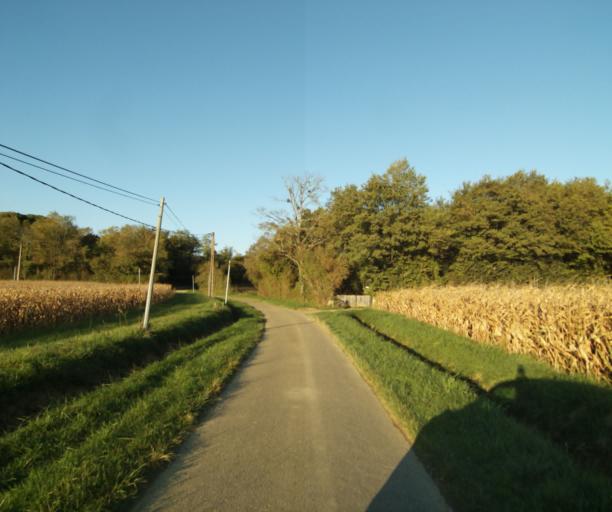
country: FR
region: Midi-Pyrenees
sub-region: Departement du Gers
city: Eauze
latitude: 43.7516
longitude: 0.1675
